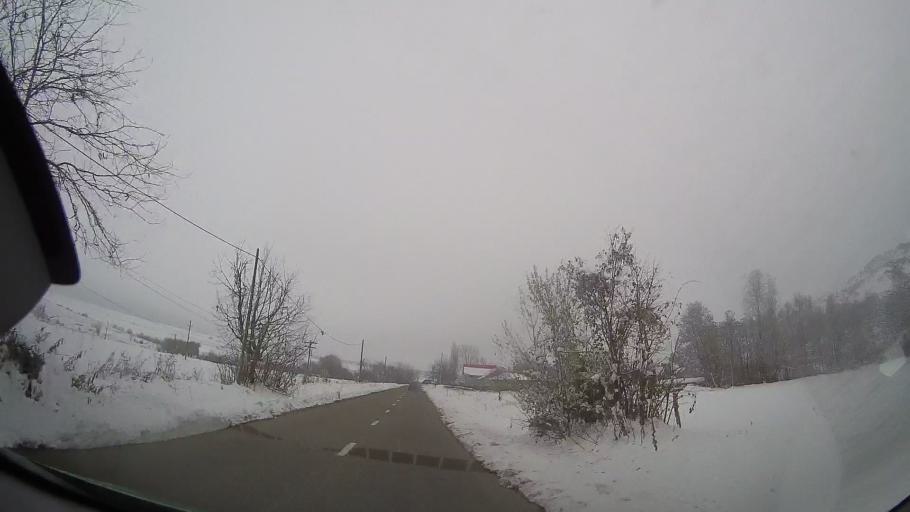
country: RO
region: Neamt
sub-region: Comuna Bozieni
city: Bozieni
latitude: 46.8321
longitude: 27.1720
